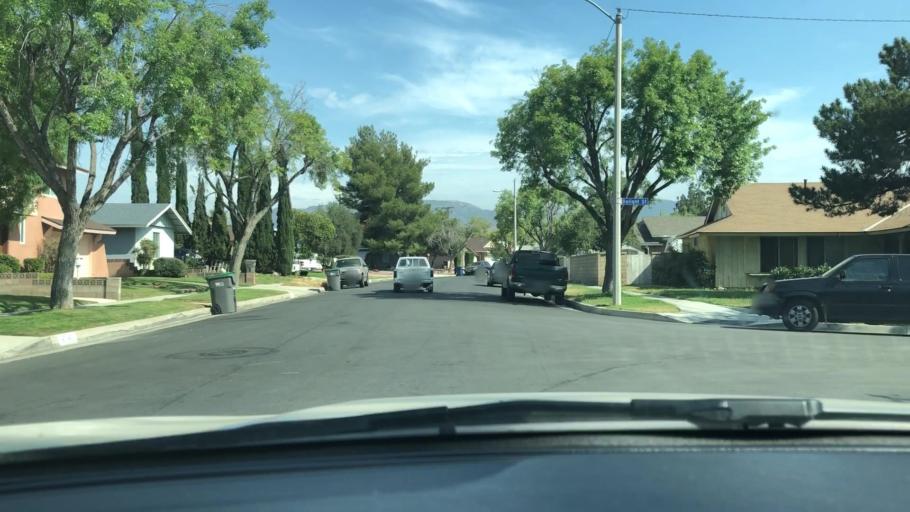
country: US
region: California
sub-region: Los Angeles County
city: Santa Clarita
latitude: 34.4242
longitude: -118.4850
